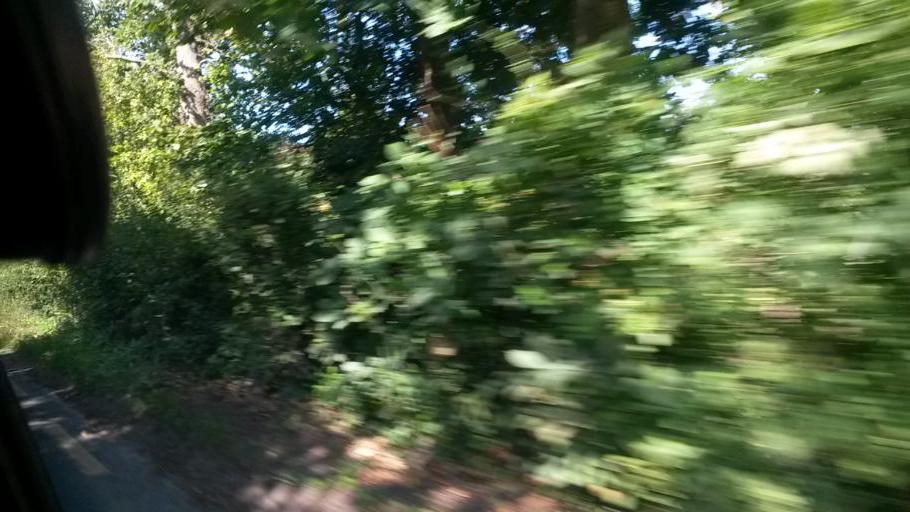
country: IE
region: Leinster
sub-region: Fingal County
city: Swords
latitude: 53.4724
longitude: -6.2728
